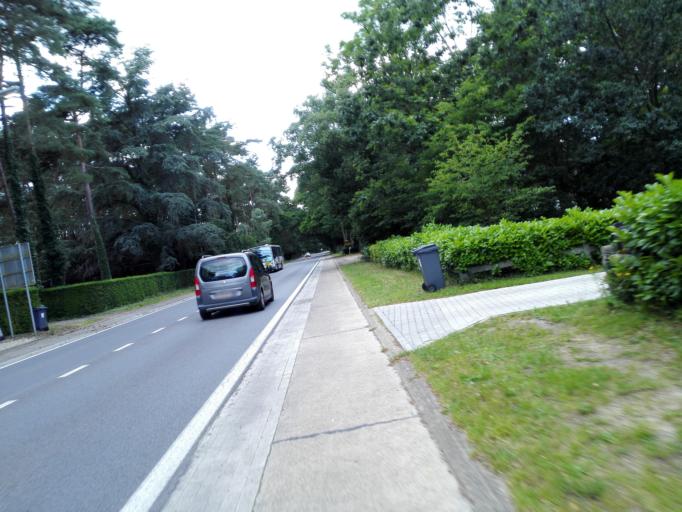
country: BE
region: Flanders
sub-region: Provincie Vlaams-Brabant
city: Keerbergen
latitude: 51.0015
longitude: 4.6461
